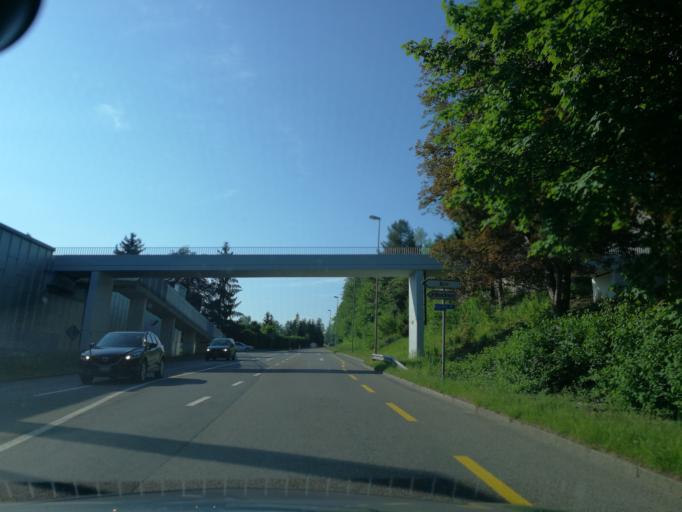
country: CH
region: Zurich
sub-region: Bezirk Horgen
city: Horgen / Allmend
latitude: 47.2456
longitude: 8.6072
